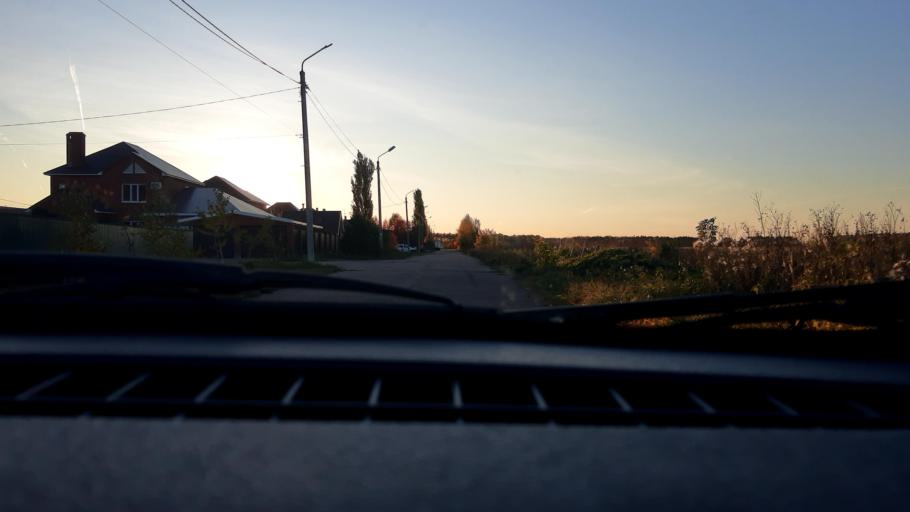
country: RU
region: Bashkortostan
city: Ufa
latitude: 54.8591
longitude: 56.0208
